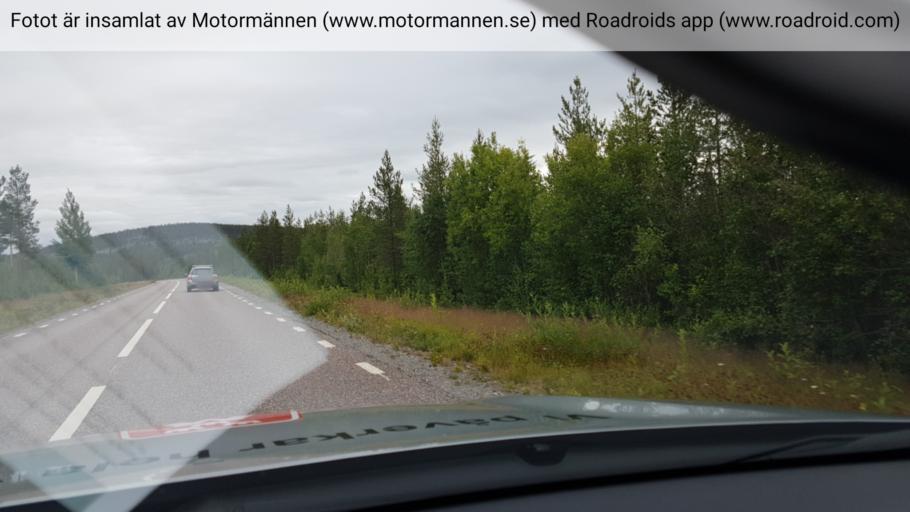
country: SE
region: Norrbotten
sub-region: Gallivare Kommun
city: Gaellivare
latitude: 67.0326
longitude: 21.7109
